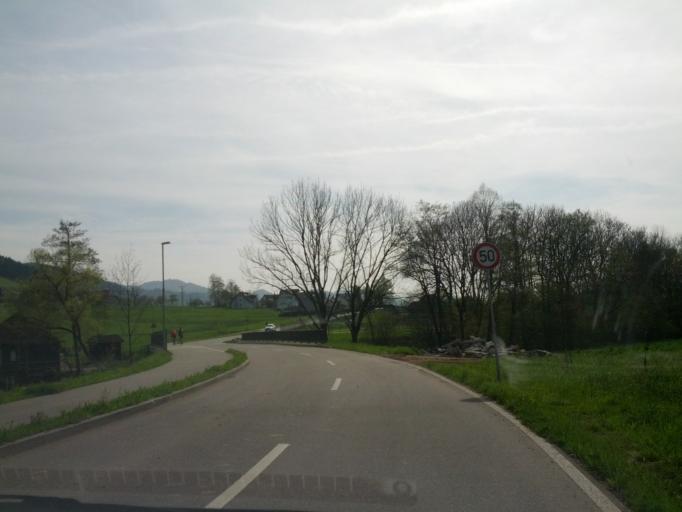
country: DE
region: Baden-Wuerttemberg
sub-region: Freiburg Region
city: Gutach im Breisgau
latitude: 48.1199
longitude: 8.0012
